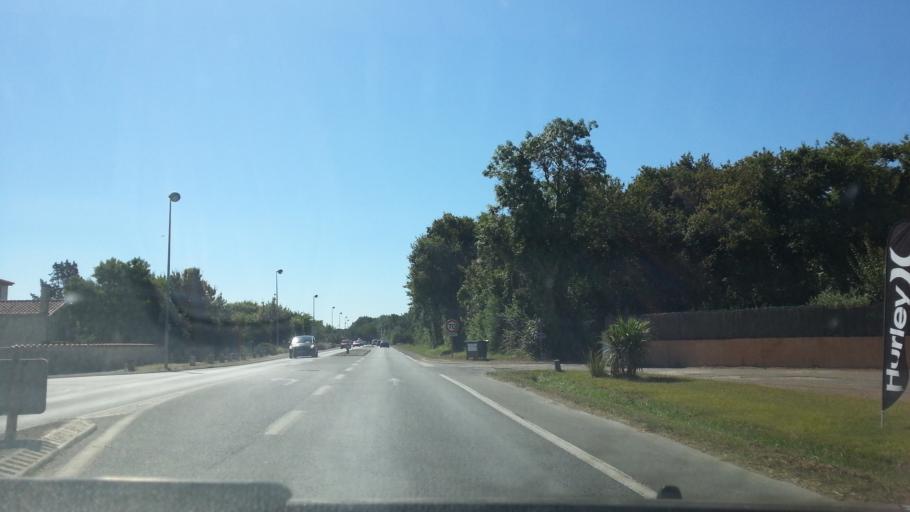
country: FR
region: Poitou-Charentes
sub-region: Departement de la Charente-Maritime
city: Dolus-d'Oleron
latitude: 45.9160
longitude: -1.2735
